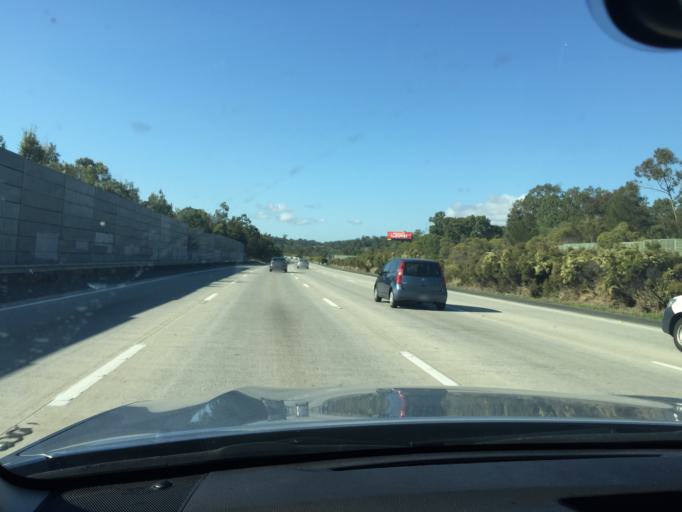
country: AU
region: Queensland
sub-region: Gold Coast
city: Ormeau Hills
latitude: -27.7925
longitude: 153.2599
